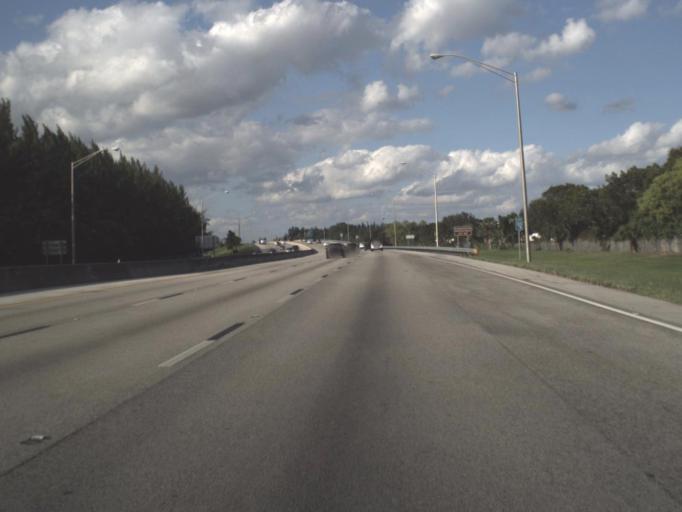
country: US
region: Florida
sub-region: Broward County
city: Coconut Creek
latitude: 26.2543
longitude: -80.1664
